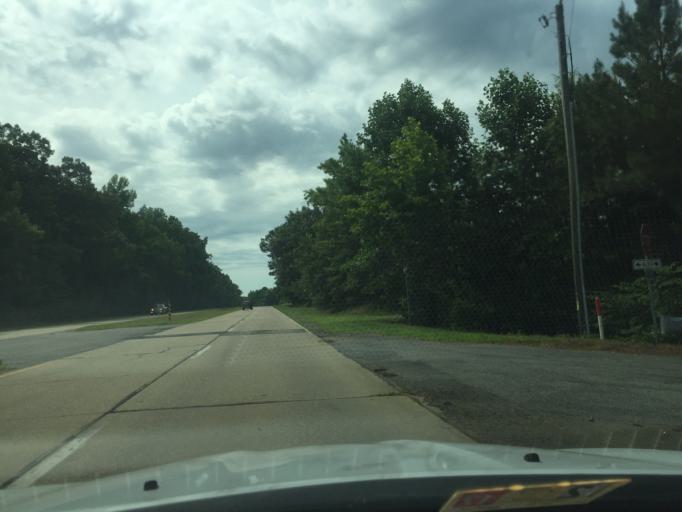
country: US
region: Virginia
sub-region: Charles City County
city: Charles City
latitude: 37.4638
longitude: -77.1047
